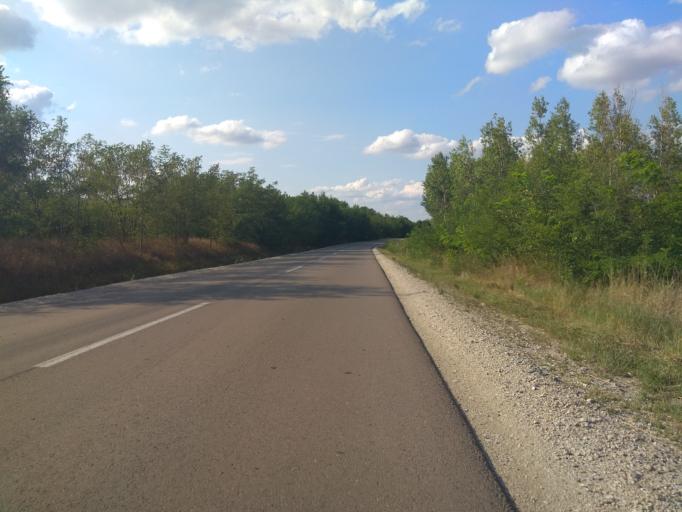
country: HU
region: Borsod-Abauj-Zemplen
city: Hejobaba
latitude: 47.8844
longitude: 20.8983
